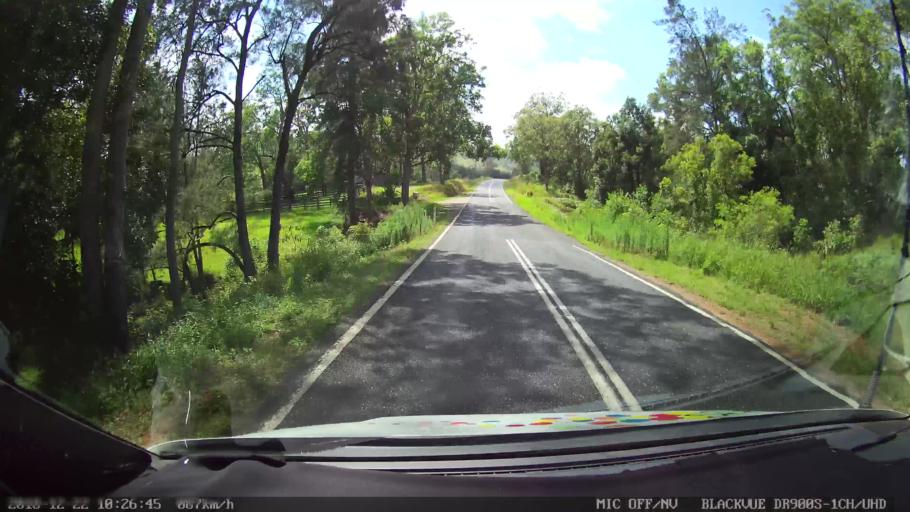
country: AU
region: New South Wales
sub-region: Clarence Valley
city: Gordon
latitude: -29.5908
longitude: 152.5739
